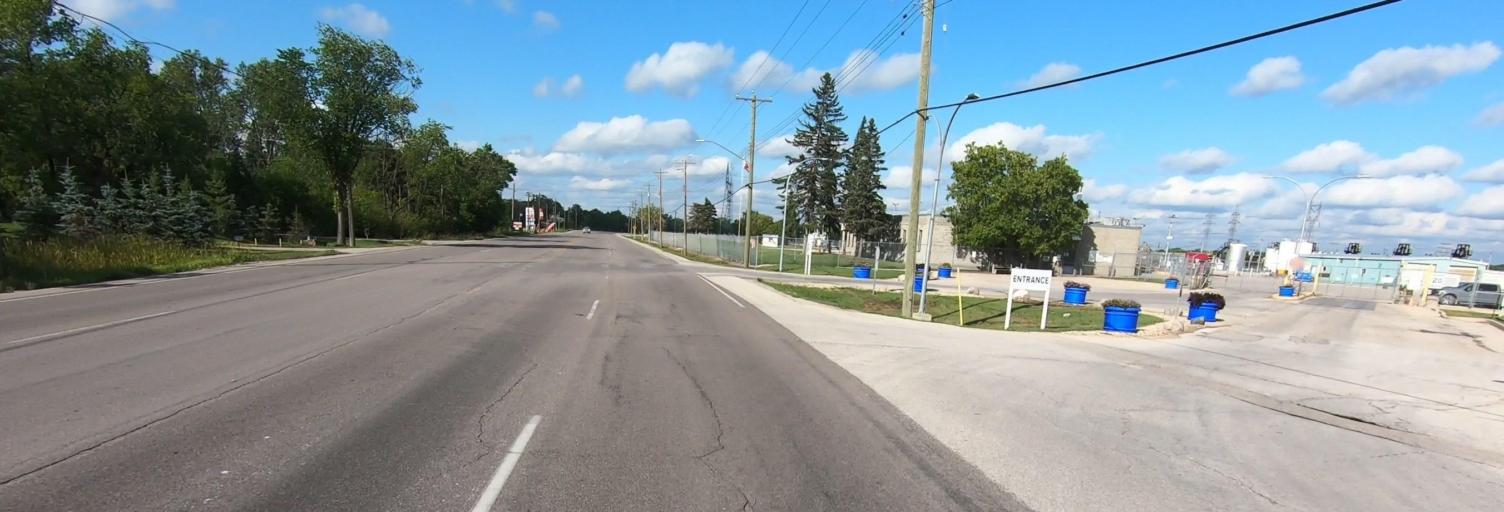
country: CA
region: Manitoba
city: Winnipeg
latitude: 49.9809
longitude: -97.0501
